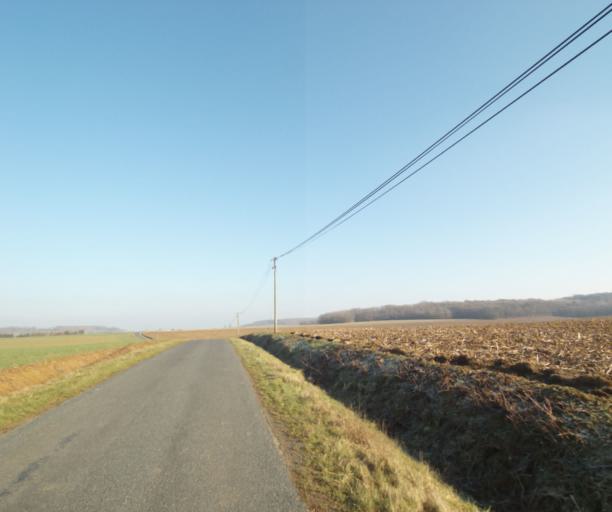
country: FR
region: Champagne-Ardenne
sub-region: Departement de la Haute-Marne
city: Bienville
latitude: 48.5299
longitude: 5.0042
